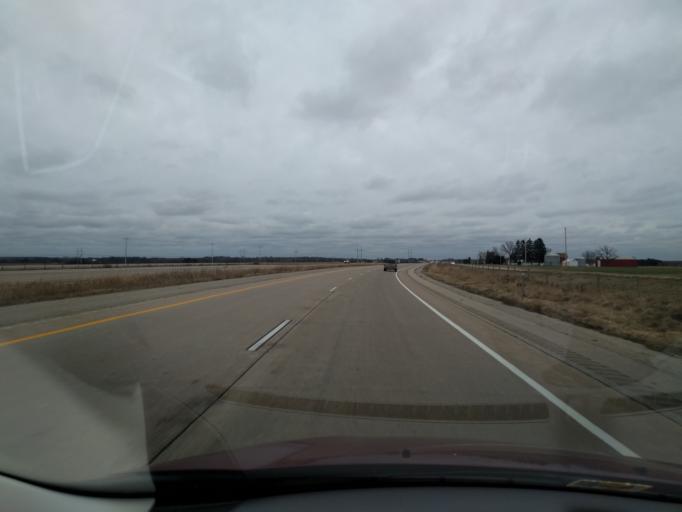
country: US
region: Wisconsin
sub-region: Winnebago County
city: Winneconne
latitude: 44.1803
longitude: -88.6647
